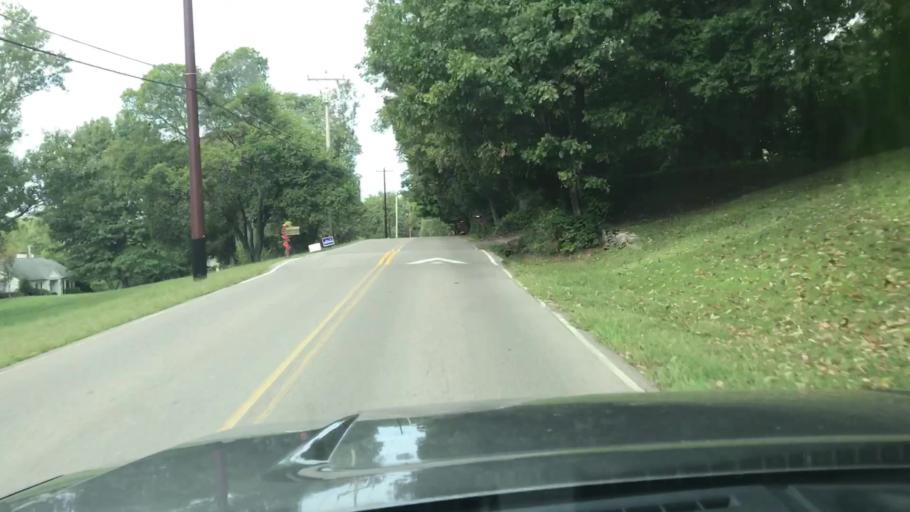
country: US
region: Tennessee
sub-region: Davidson County
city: Forest Hills
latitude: 36.0662
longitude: -86.8174
